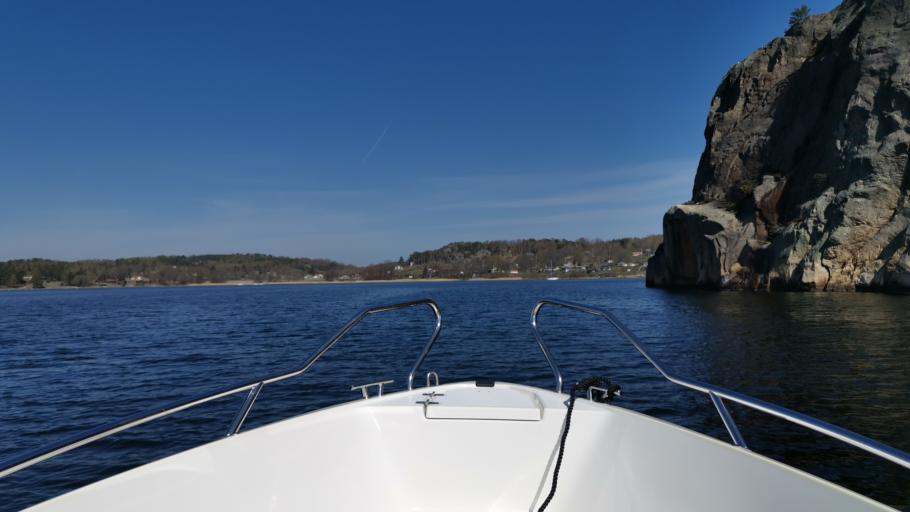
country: SE
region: Vaestra Goetaland
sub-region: Orust
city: Henan
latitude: 58.2540
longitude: 11.5737
